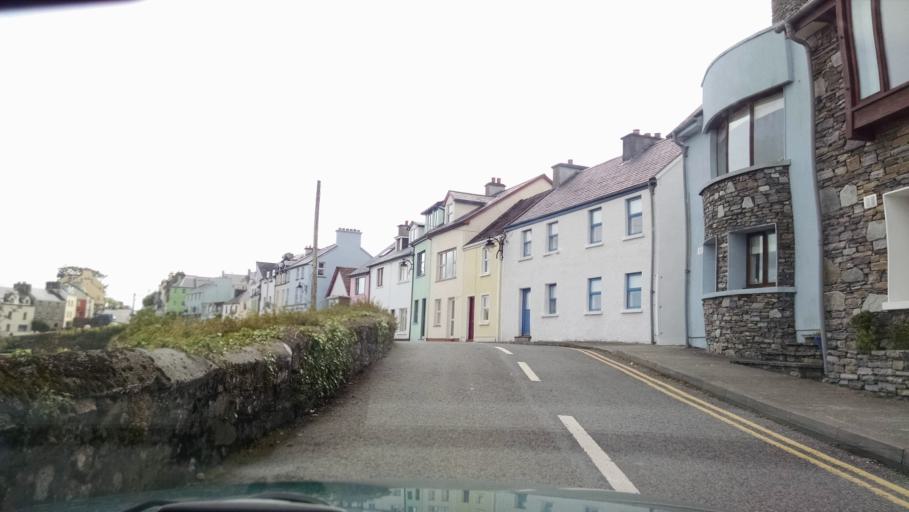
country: IE
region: Connaught
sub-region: County Galway
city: Clifden
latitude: 53.3979
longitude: -9.9190
